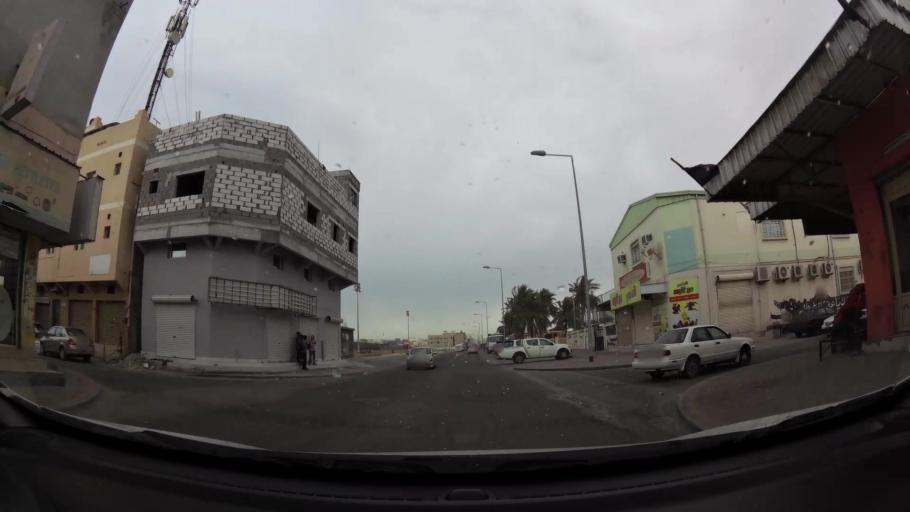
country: BH
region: Central Governorate
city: Madinat Hamad
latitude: 26.0996
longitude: 50.4852
